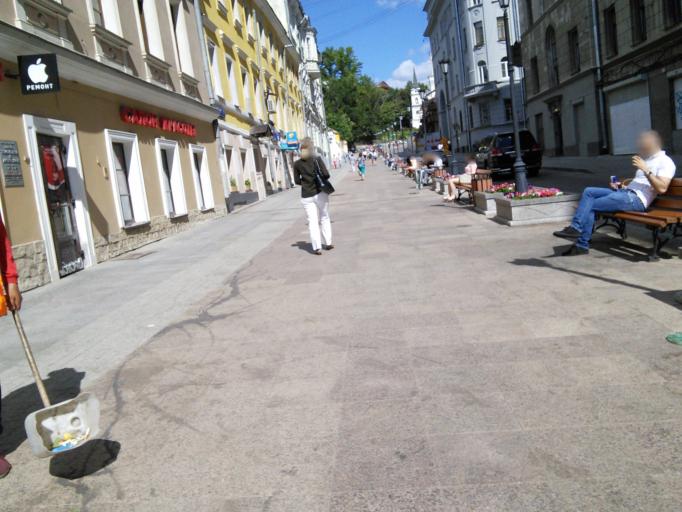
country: RU
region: Moscow
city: Zamoskvorech'ye
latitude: 55.7544
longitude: 37.6373
